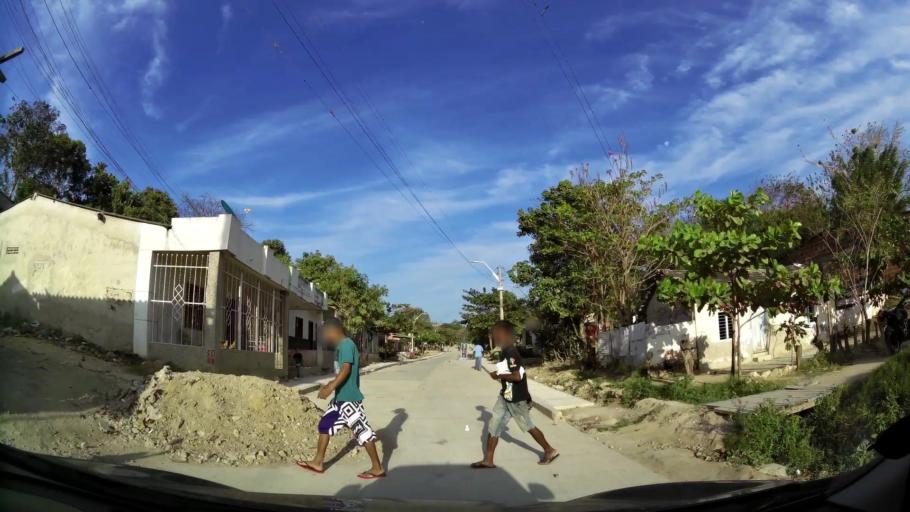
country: CO
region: Atlantico
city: Barranquilla
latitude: 10.9548
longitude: -74.8139
